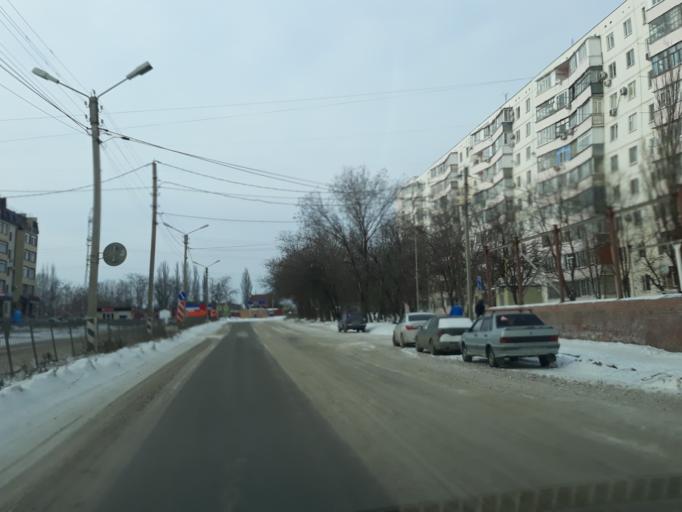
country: RU
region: Rostov
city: Taganrog
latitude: 47.2236
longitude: 38.8590
